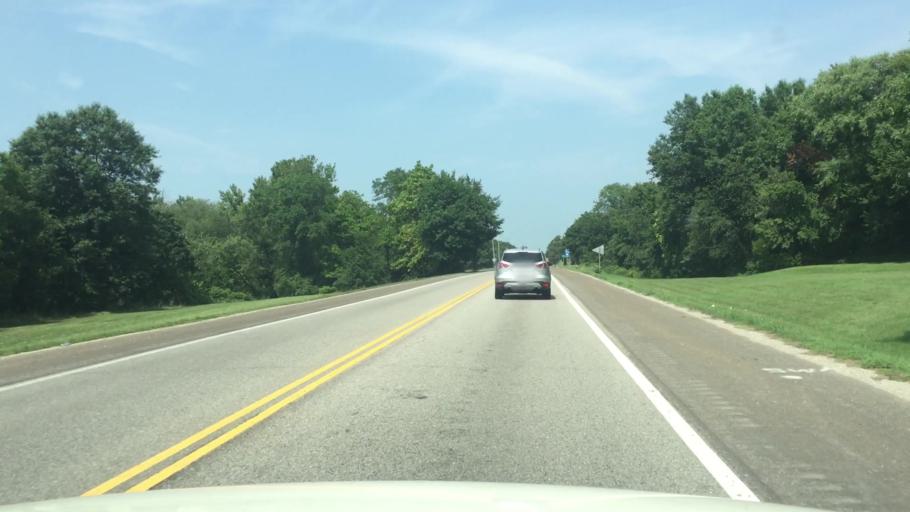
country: US
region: Kansas
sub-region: Crawford County
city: Pittsburg
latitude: 37.4159
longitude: -94.7219
